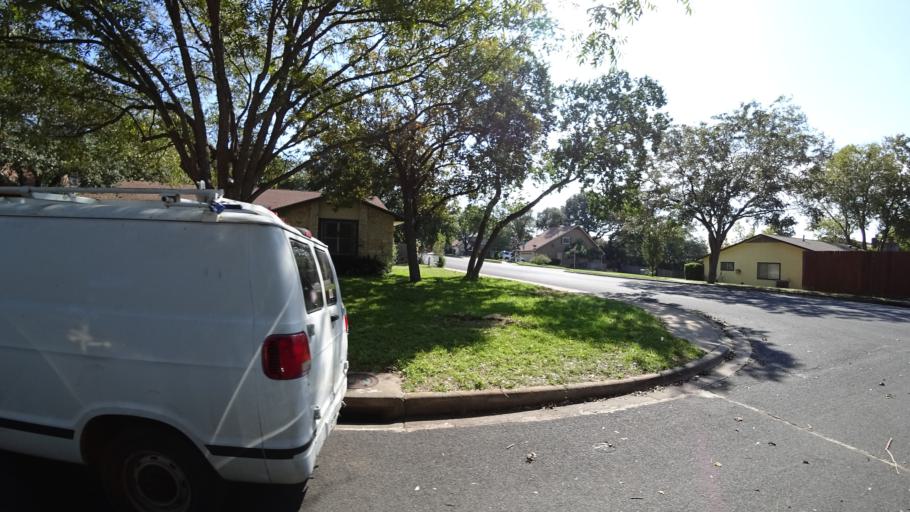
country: US
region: Texas
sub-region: Travis County
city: Shady Hollow
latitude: 30.1963
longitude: -97.8156
